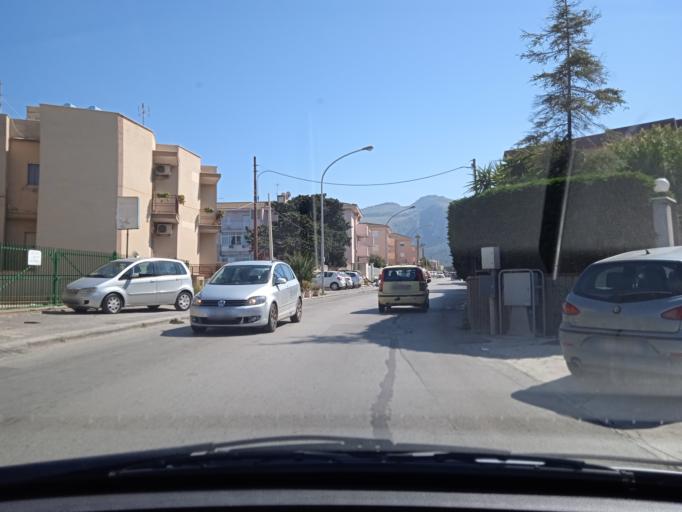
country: IT
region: Sicily
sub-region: Palermo
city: Villabate
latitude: 38.0905
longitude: 13.4324
